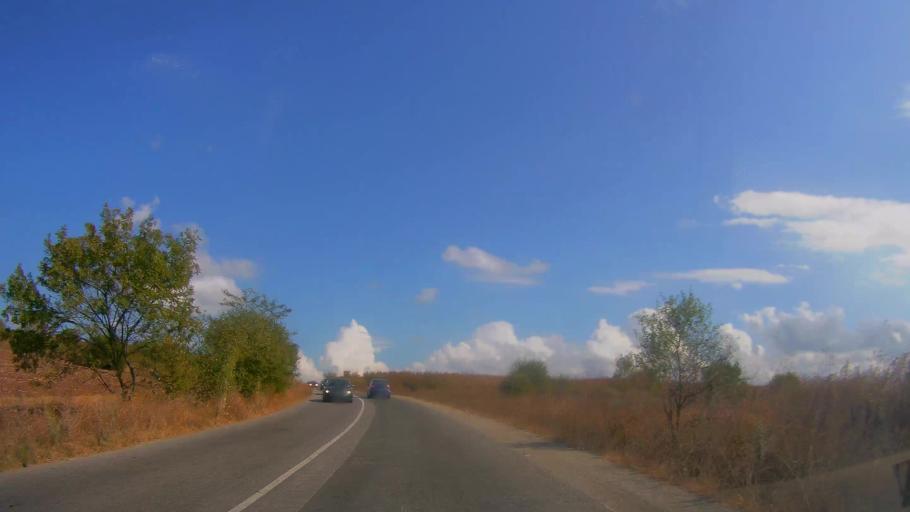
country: BG
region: Burgas
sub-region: Obshtina Burgas
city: Burgas
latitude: 42.4772
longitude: 27.3908
